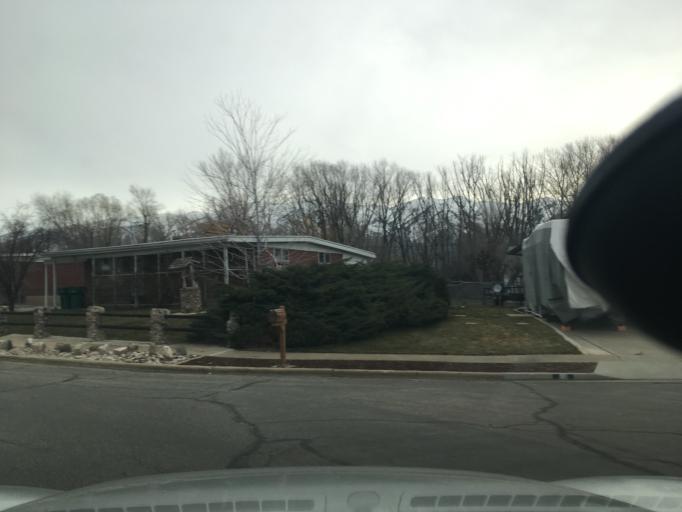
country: US
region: Utah
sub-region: Davis County
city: Layton
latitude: 41.0617
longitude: -111.9635
